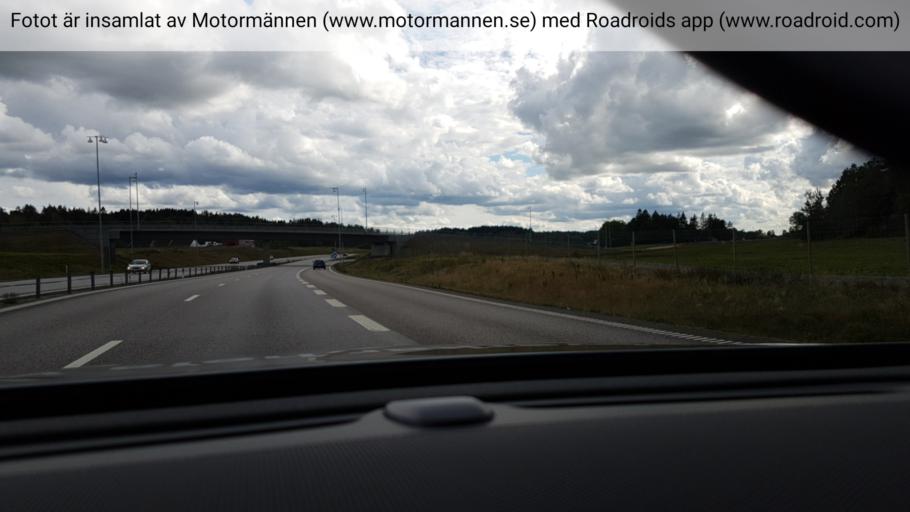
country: SE
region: Vaestra Goetaland
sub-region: Lilla Edets Kommun
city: Lodose
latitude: 58.0407
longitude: 12.1767
